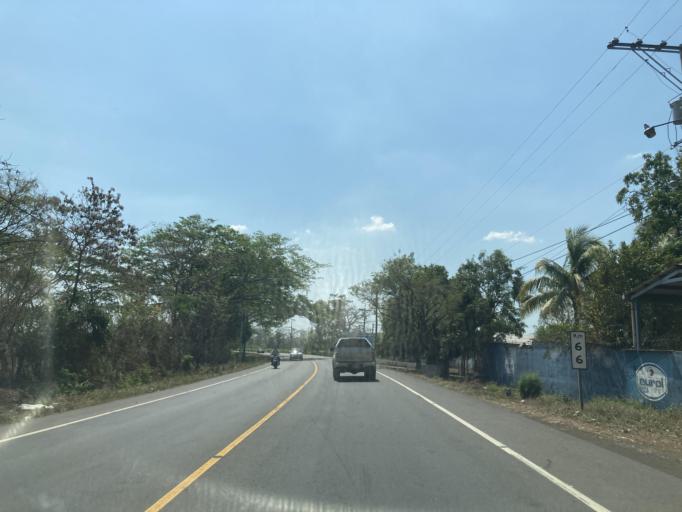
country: GT
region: Escuintla
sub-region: Municipio de Escuintla
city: Escuintla
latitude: 14.2371
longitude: -90.7418
